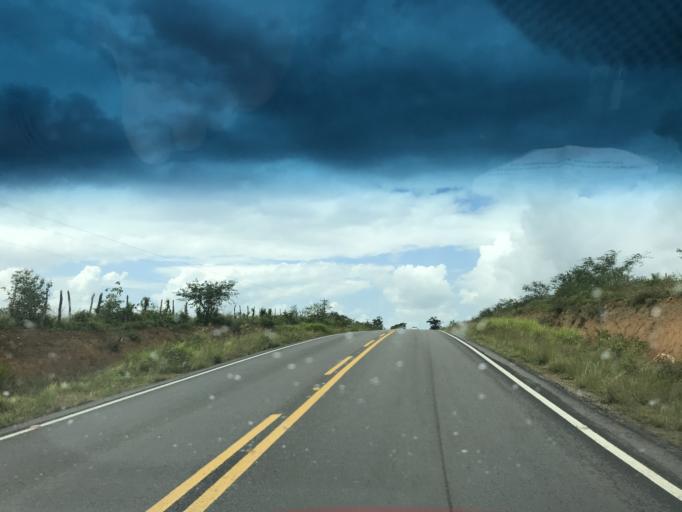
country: BR
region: Bahia
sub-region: Conceicao Do Almeida
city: Conceicao do Almeida
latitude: -12.6756
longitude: -39.2647
